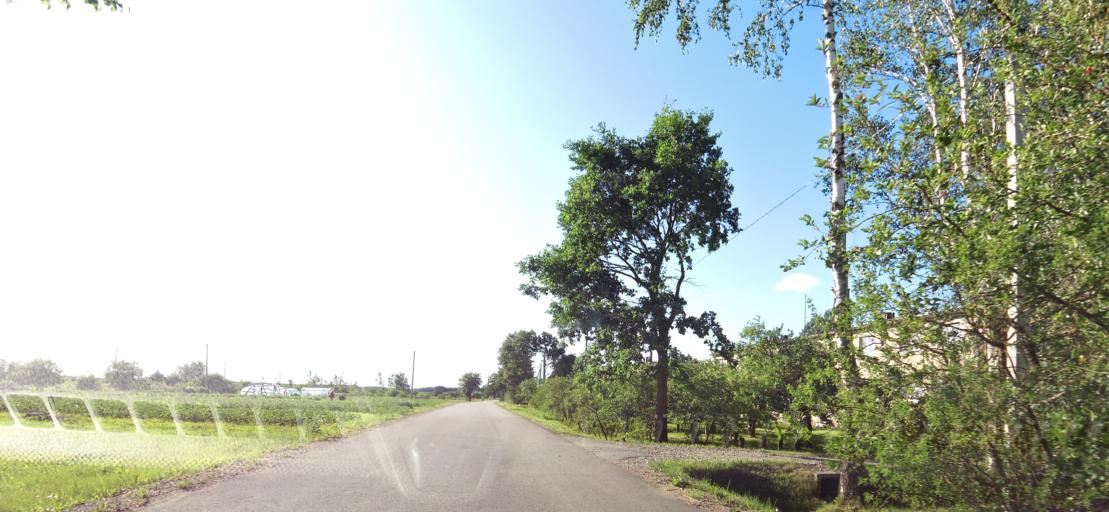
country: LT
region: Panevezys
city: Pasvalys
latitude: 56.1335
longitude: 24.5399
